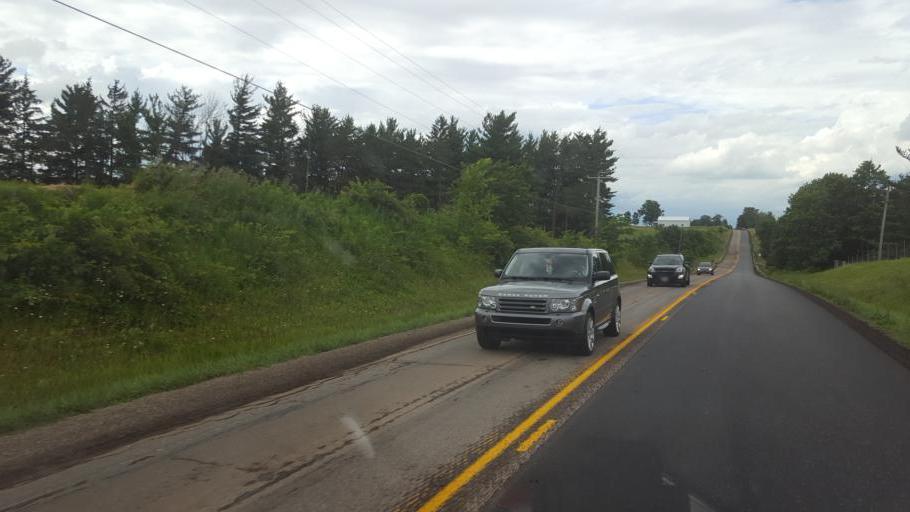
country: US
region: Ohio
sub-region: Richland County
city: Lexington
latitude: 40.6039
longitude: -82.6624
